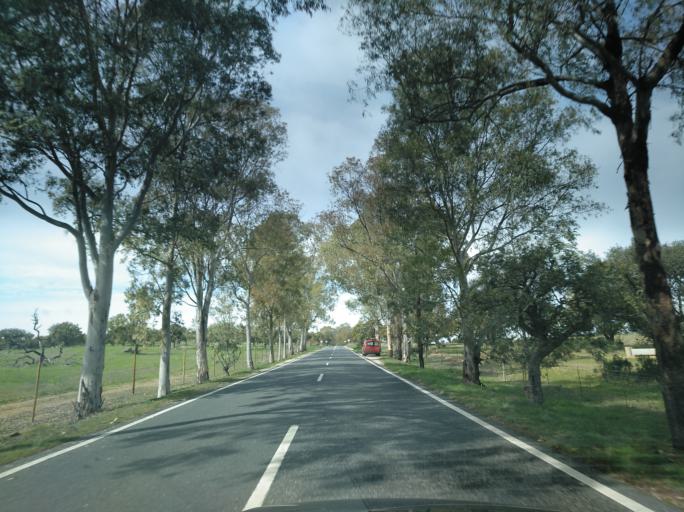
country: PT
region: Beja
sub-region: Mertola
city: Mertola
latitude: 37.7309
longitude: -7.7682
